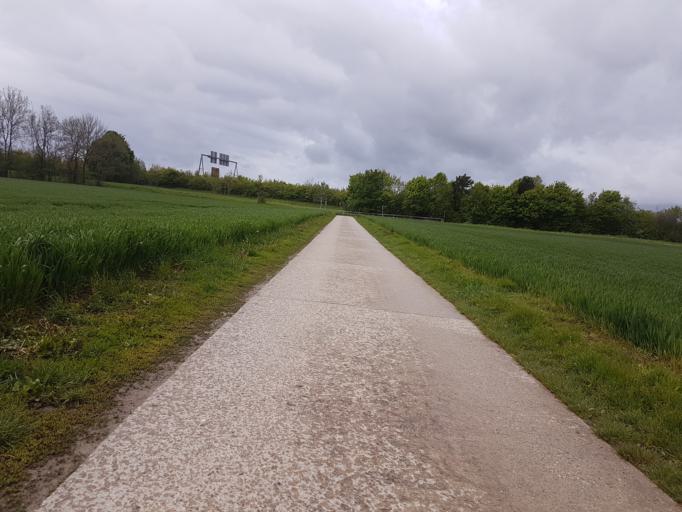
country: CH
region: Vaud
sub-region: Jura-Nord vaudois District
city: Chavornay
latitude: 46.7231
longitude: 6.5725
